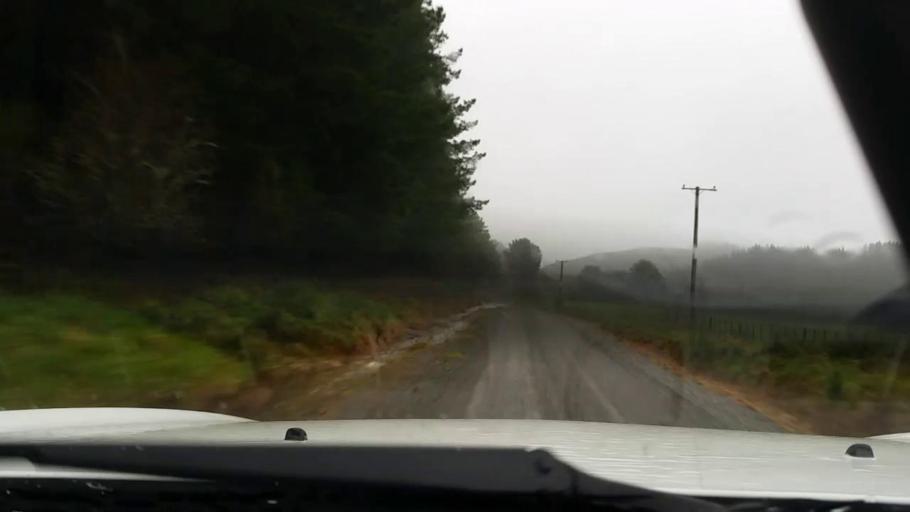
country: NZ
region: Wellington
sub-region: Masterton District
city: Masterton
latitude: -41.1803
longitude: 175.8288
